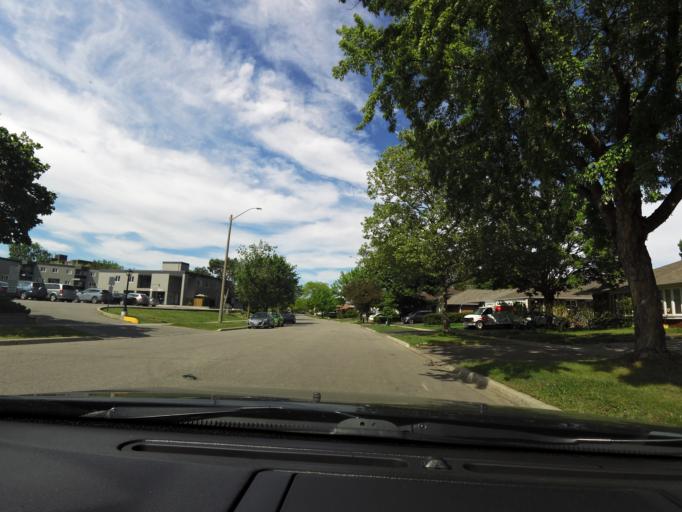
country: CA
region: Ontario
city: Mississauga
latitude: 43.5089
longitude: -79.6254
